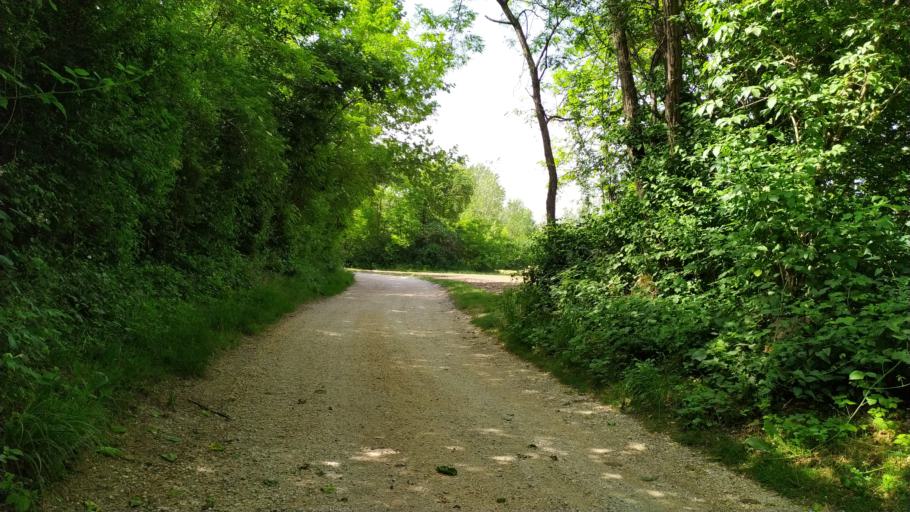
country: IT
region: Veneto
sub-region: Provincia di Treviso
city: Sernaglia della Battaglia
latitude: 45.8621
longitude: 12.1409
